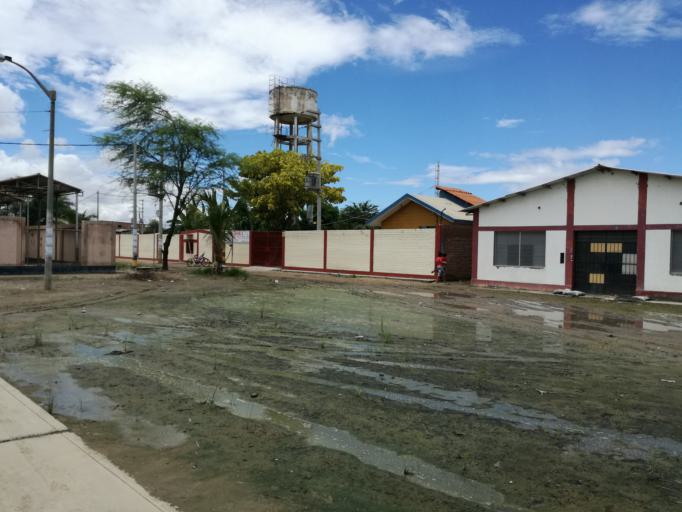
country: PE
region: Piura
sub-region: Provincia de Piura
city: Catacaos
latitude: -5.2473
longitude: -80.6517
